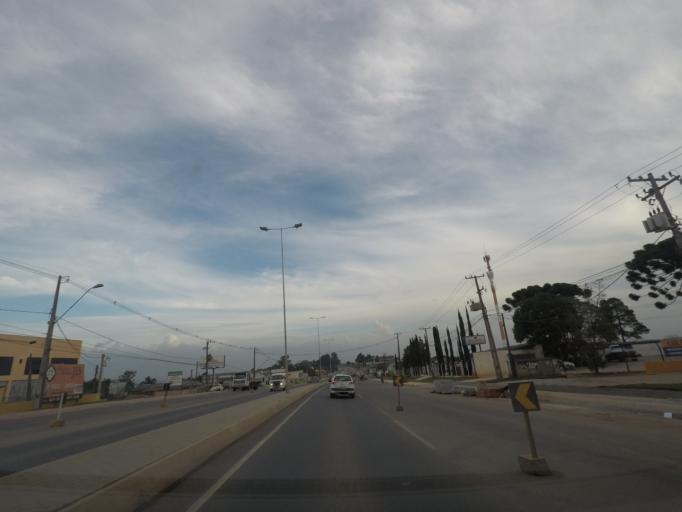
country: BR
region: Parana
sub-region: Colombo
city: Colombo
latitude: -25.3318
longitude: -49.2209
